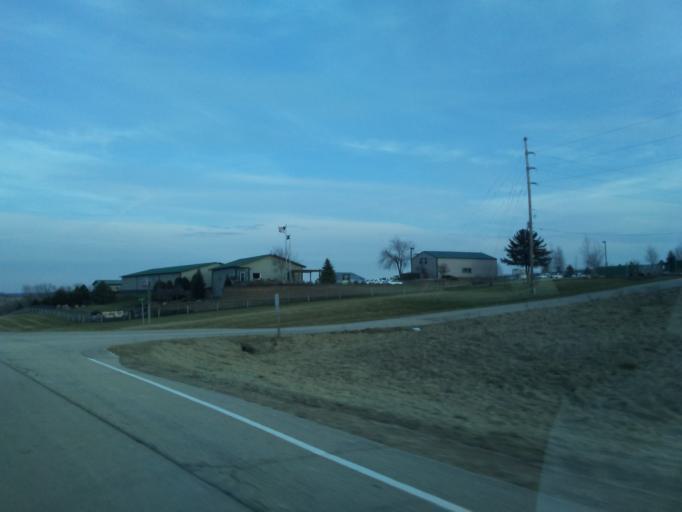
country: US
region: Wisconsin
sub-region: Dane County
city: Verona
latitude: 42.9879
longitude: -89.6029
